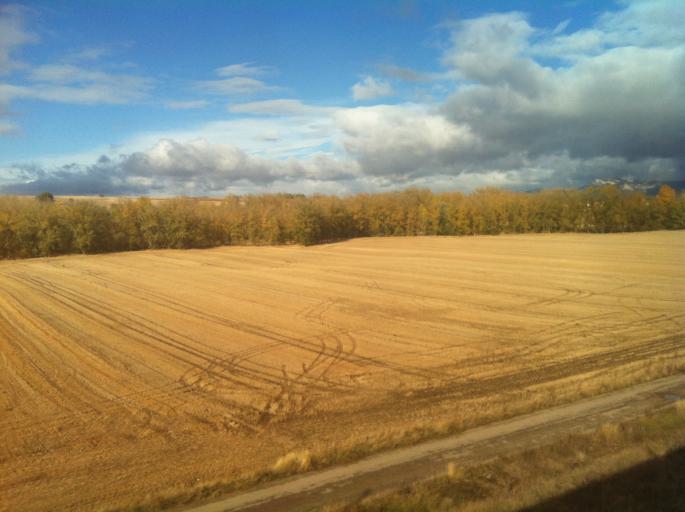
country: ES
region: Castille and Leon
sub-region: Provincia de Burgos
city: Aguilar de Bureba
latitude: 42.5828
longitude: -3.2989
